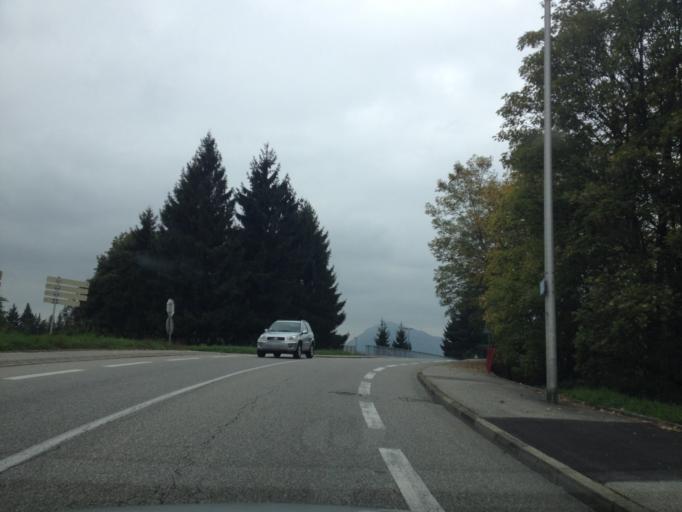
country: FR
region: Rhone-Alpes
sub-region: Departement de la Haute-Savoie
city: Cran-Gevrier
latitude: 45.8994
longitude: 6.1027
